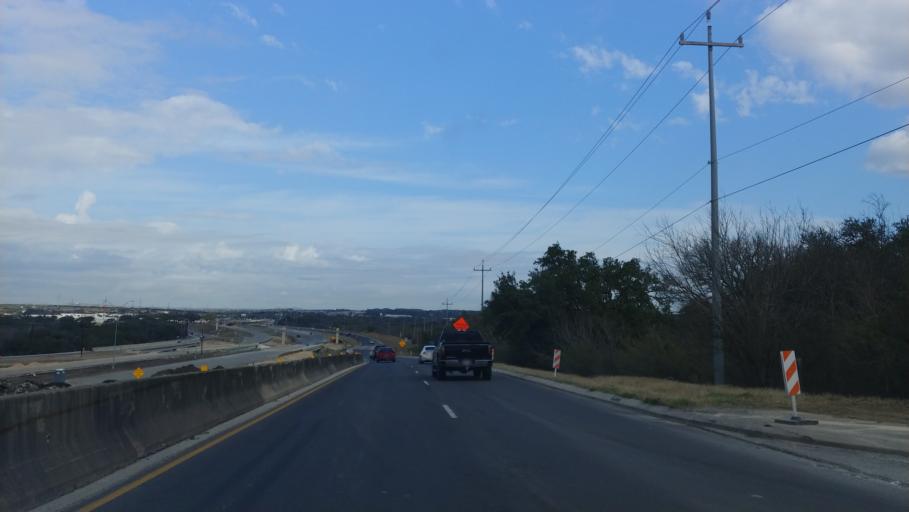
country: US
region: Texas
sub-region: Bexar County
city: Lackland Air Force Base
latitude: 29.4170
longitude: -98.7091
